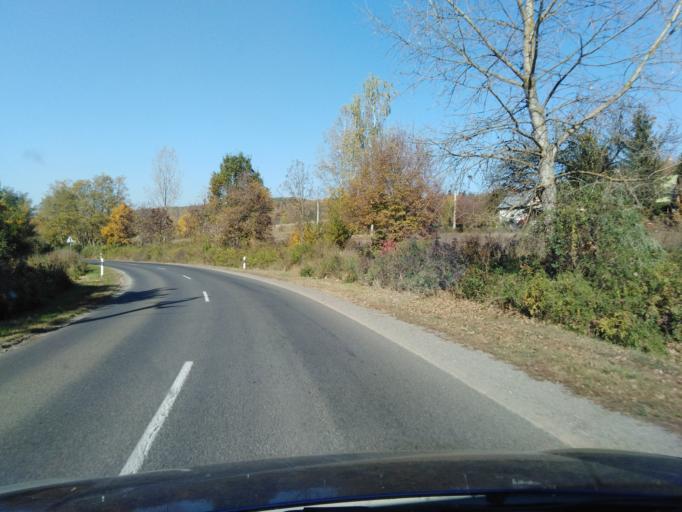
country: HU
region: Nograd
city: Salgotarjan
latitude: 48.1242
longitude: 19.7766
